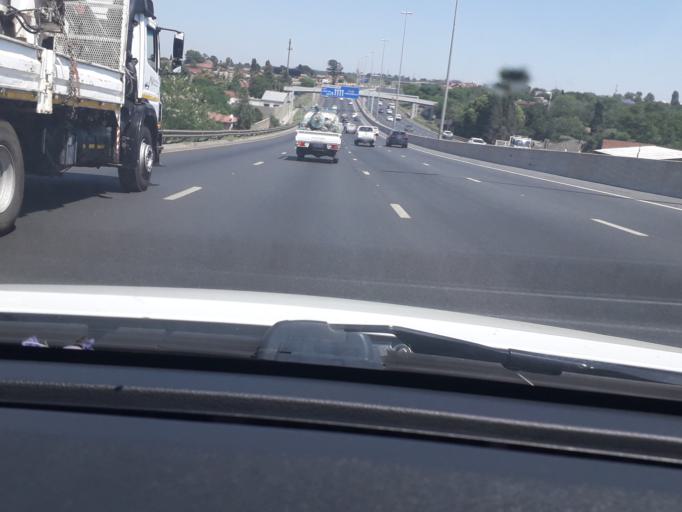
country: ZA
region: Gauteng
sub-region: Ekurhuleni Metropolitan Municipality
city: Boksburg
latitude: -26.1803
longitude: 28.2078
